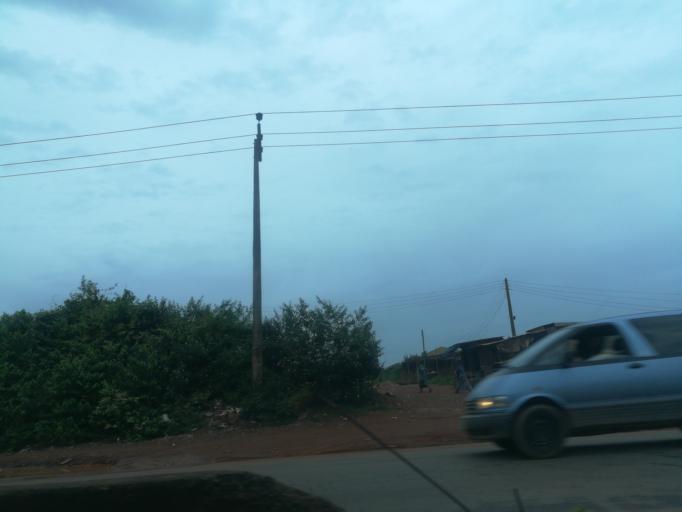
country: NG
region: Oyo
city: Ibadan
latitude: 7.3900
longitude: 3.9772
